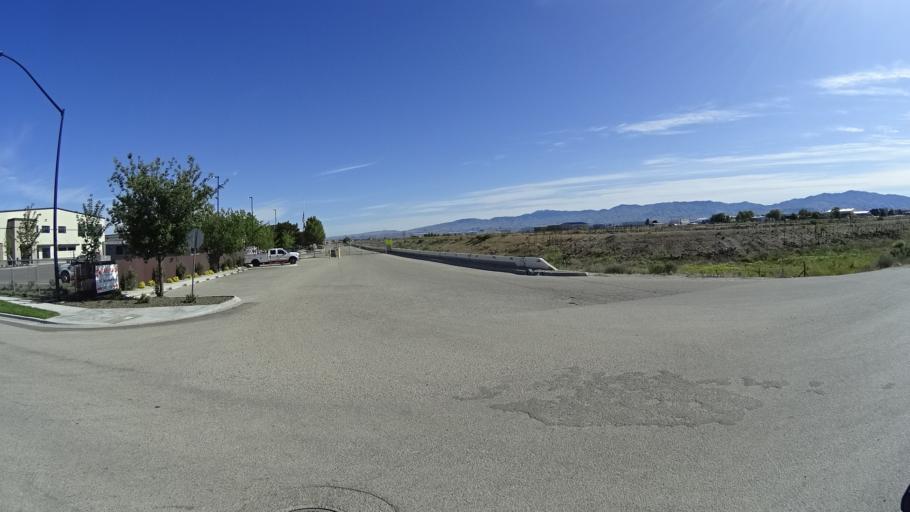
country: US
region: Idaho
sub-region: Ada County
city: Garden City
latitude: 43.5573
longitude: -116.2487
